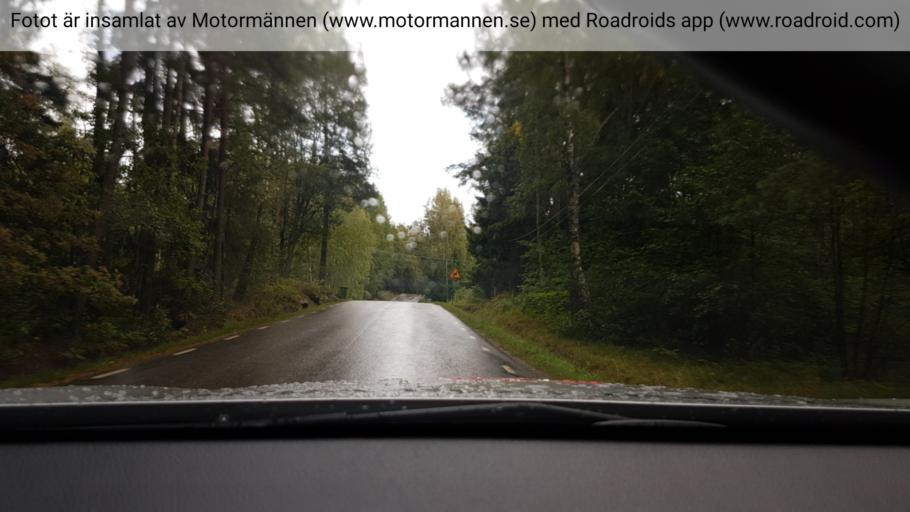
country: SE
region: Stockholm
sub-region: Haninge Kommun
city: Jordbro
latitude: 59.0765
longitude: 18.0557
